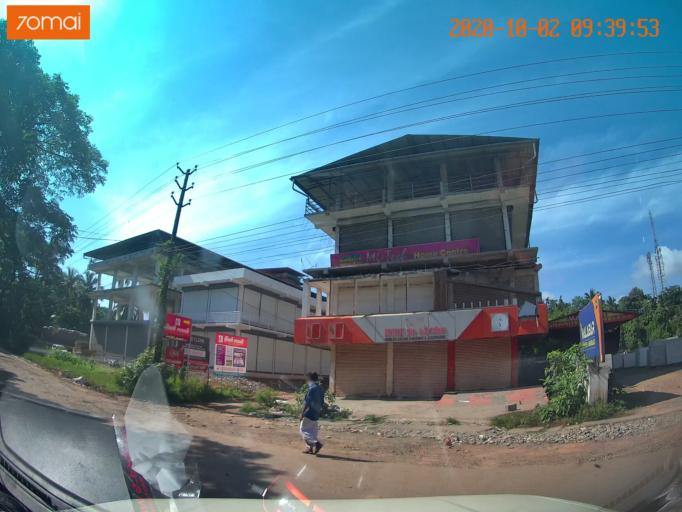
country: IN
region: Kerala
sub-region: Kozhikode
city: Nadapuram
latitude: 11.6539
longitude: 75.7558
